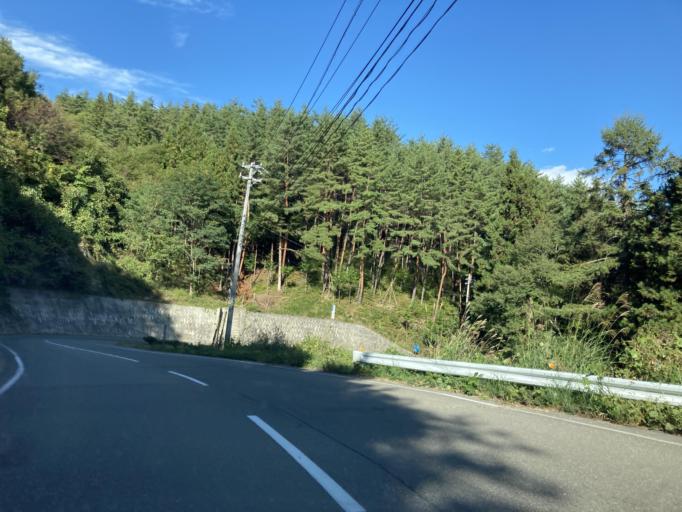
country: JP
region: Nagano
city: Omachi
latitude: 36.4878
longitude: 137.9030
